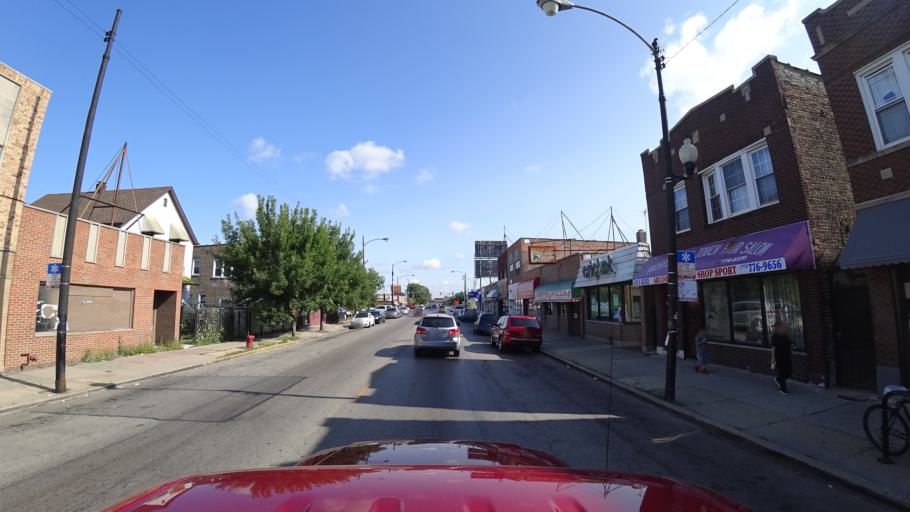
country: US
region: Illinois
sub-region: Cook County
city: Cicero
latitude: 41.7997
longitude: -87.7037
